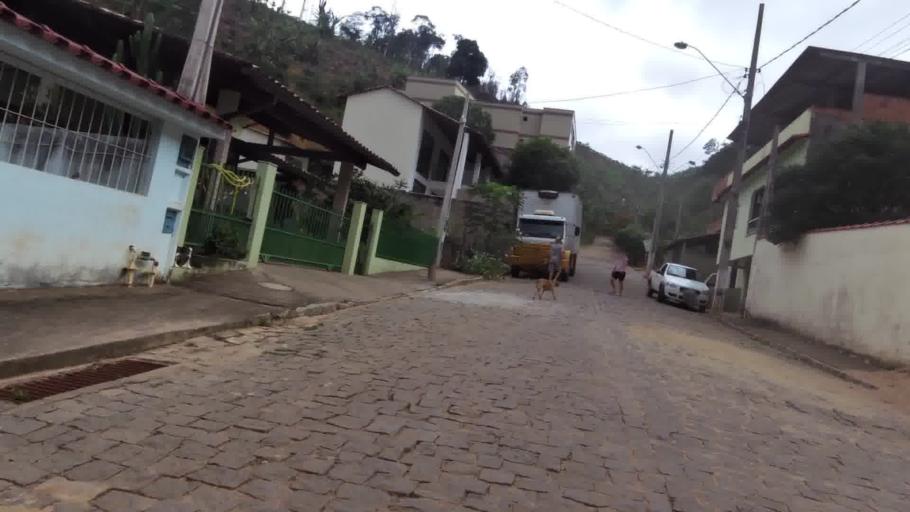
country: BR
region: Espirito Santo
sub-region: Alfredo Chaves
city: Alfredo Chaves
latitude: -20.6375
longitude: -40.7553
